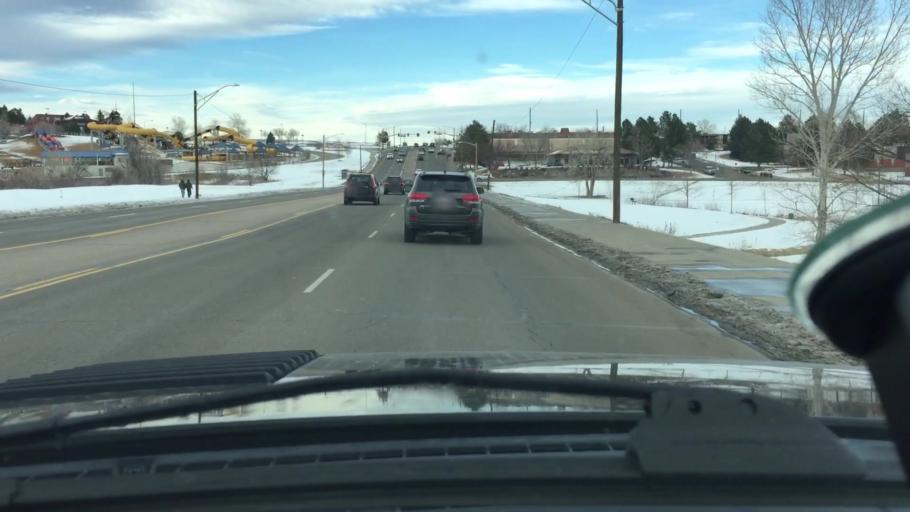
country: US
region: Colorado
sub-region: Adams County
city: Federal Heights
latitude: 39.8529
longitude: -105.0060
